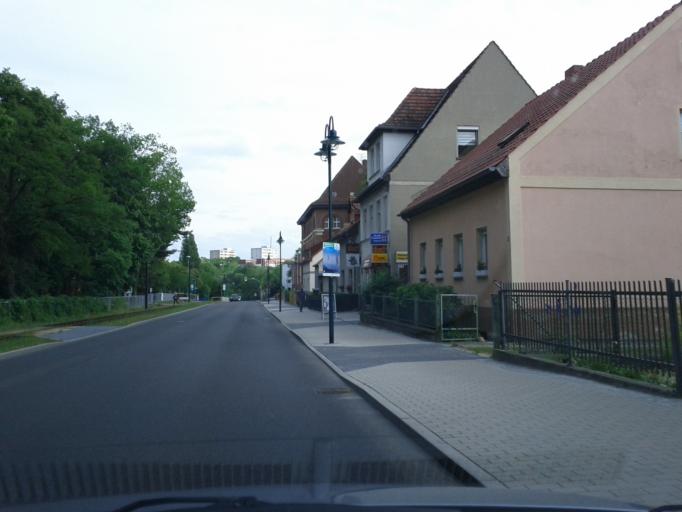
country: DE
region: Brandenburg
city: Woltersdorf
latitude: 52.4712
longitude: 13.7851
